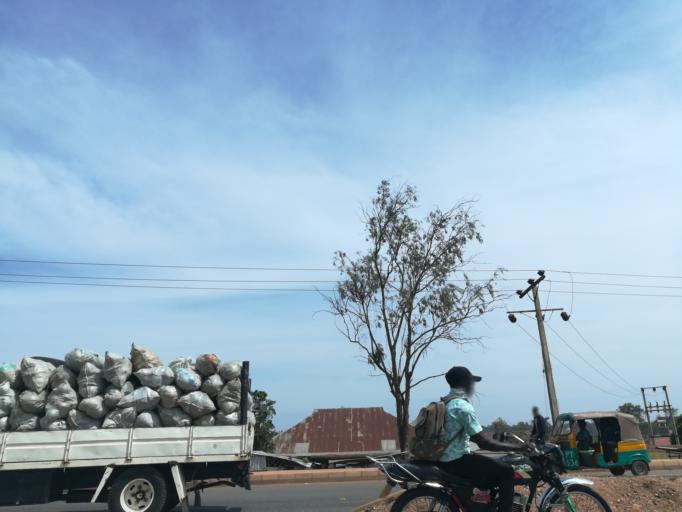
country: NG
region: Plateau
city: Bukuru
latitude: 9.7630
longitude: 8.8597
